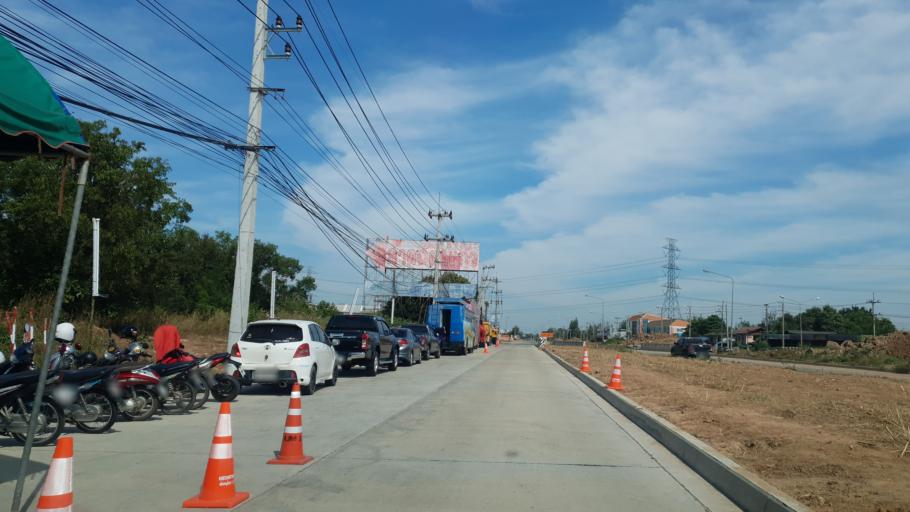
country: TH
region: Phitsanulok
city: Phitsanulok
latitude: 16.8197
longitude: 100.3302
